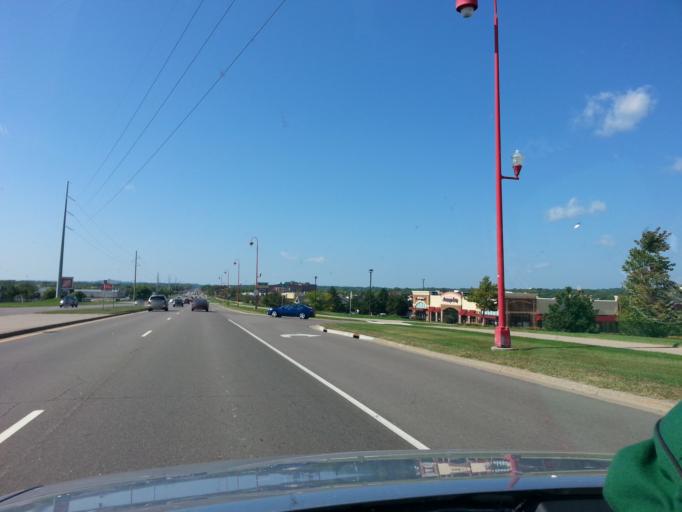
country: US
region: Minnesota
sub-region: Dakota County
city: Apple Valley
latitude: 44.7320
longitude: -93.1991
